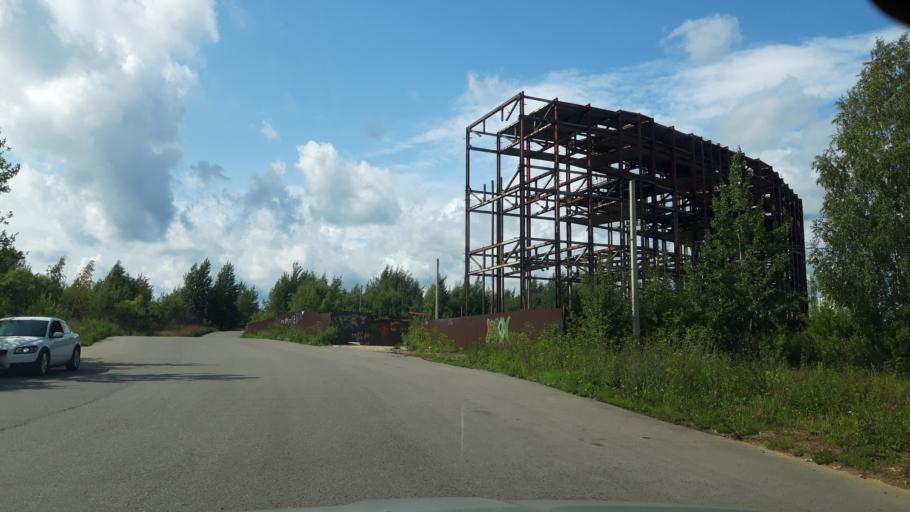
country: RU
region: Moscow
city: Zelenograd
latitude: 55.9646
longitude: 37.1716
